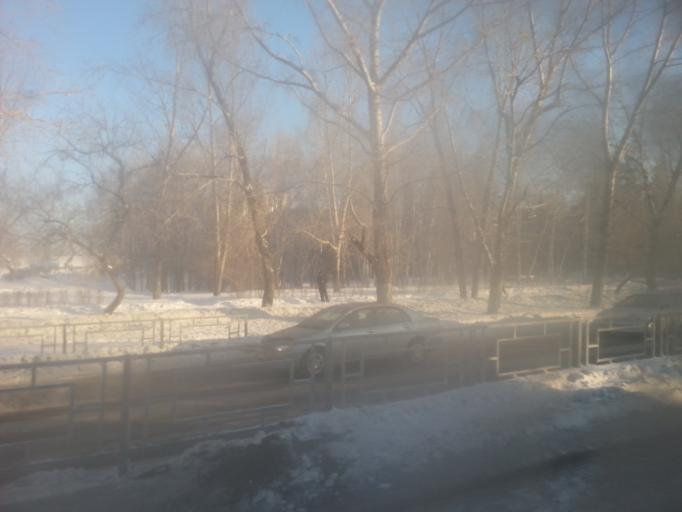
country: RU
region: Altai Krai
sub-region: Gorod Barnaulskiy
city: Barnaul
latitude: 53.3572
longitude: 83.7095
